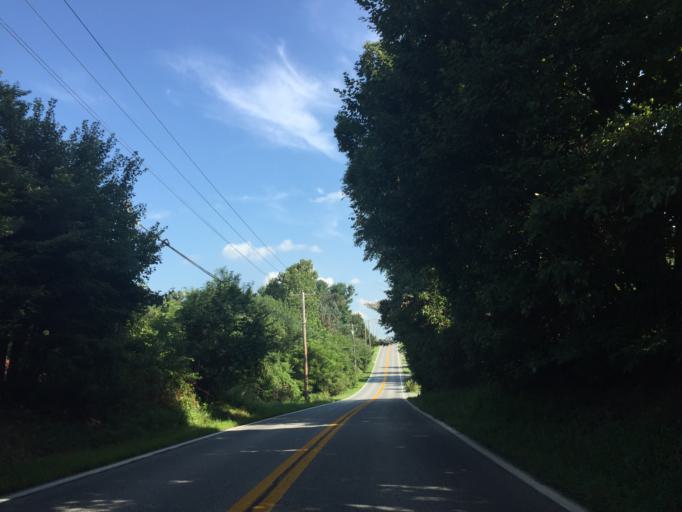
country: US
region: Maryland
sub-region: Carroll County
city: Hampstead
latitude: 39.6390
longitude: -76.7991
